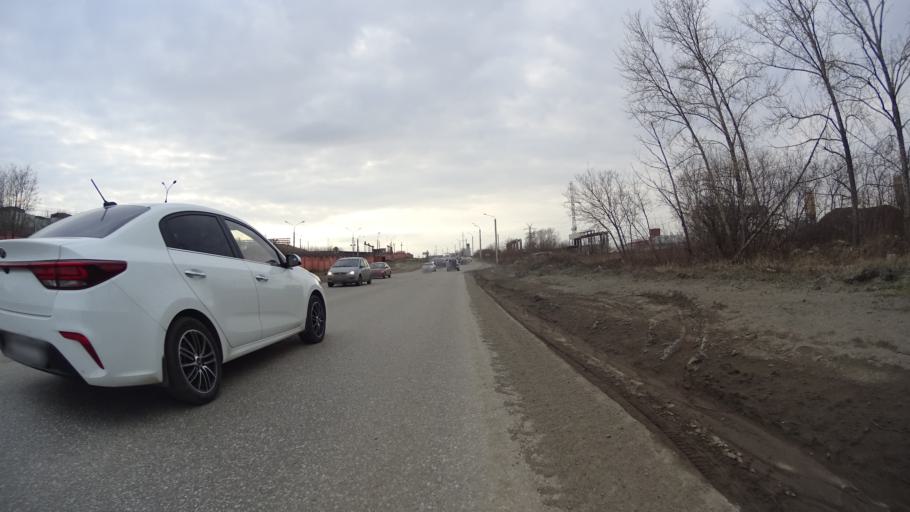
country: RU
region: Chelyabinsk
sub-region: Gorod Chelyabinsk
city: Chelyabinsk
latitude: 55.1575
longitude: 61.4898
